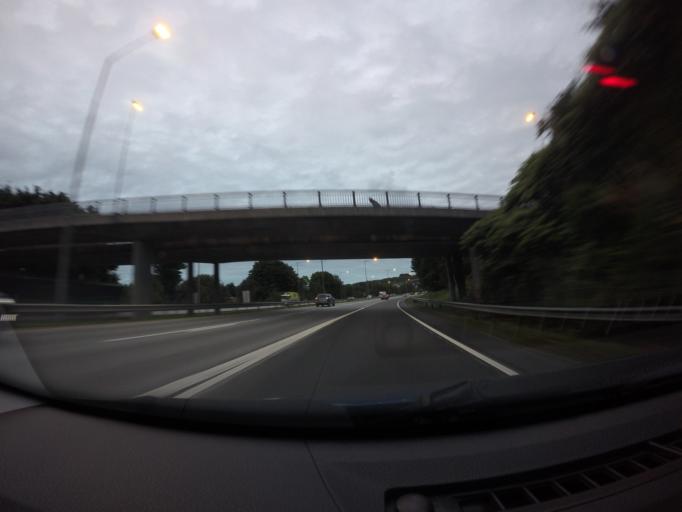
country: NO
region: Rogaland
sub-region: Stavanger
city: Stavanger
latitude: 58.9415
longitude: 5.7251
